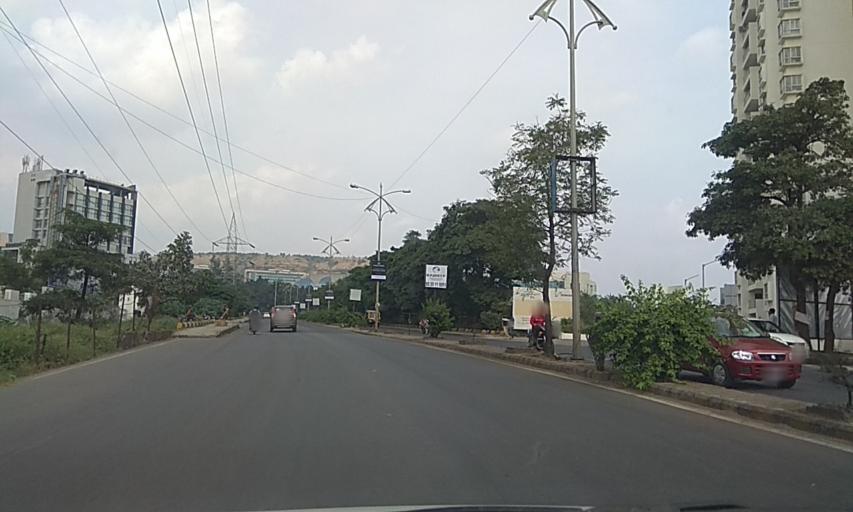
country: IN
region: Maharashtra
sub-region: Pune Division
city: Pimpri
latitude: 18.5913
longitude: 73.7070
